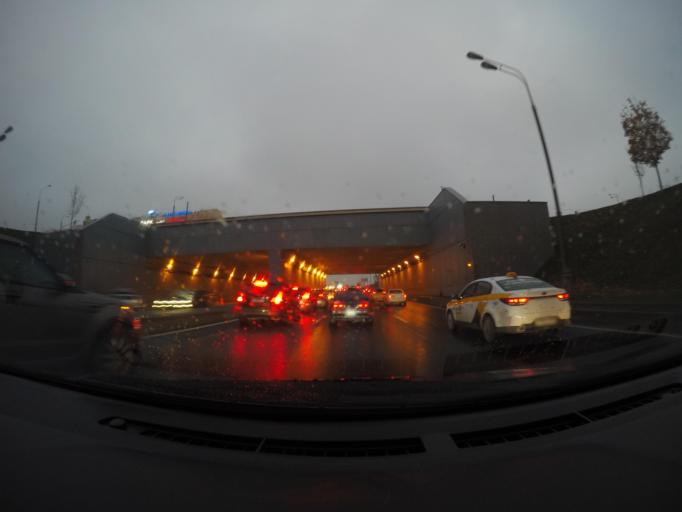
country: RU
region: Moscow
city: Chertanovo Yuzhnoye
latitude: 55.6097
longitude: 37.6090
